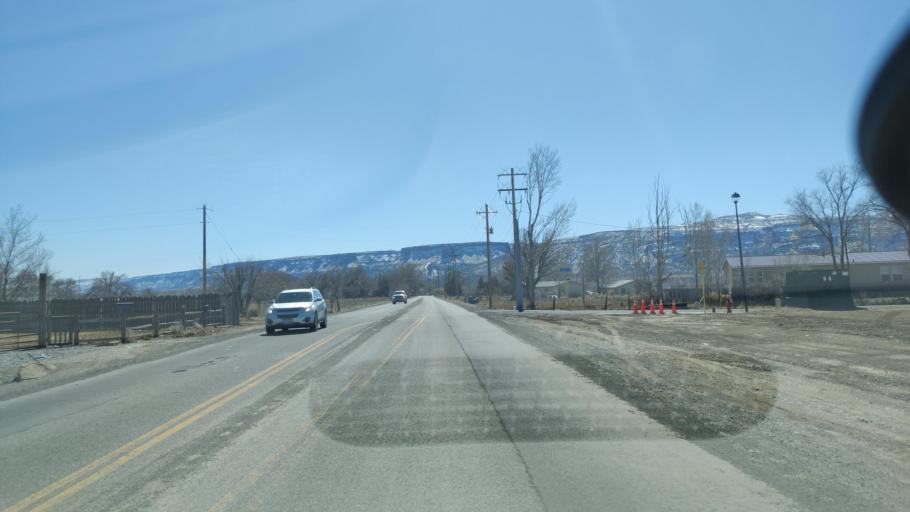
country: US
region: Colorado
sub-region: Mesa County
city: Fruita
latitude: 39.1431
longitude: -108.7012
